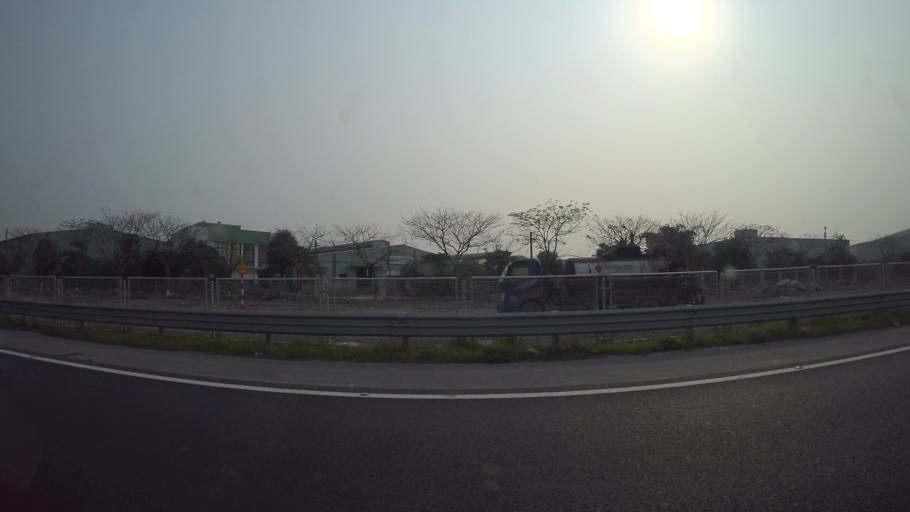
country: VN
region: Ha Noi
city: Thuong Tin
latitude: 20.8771
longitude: 105.8751
